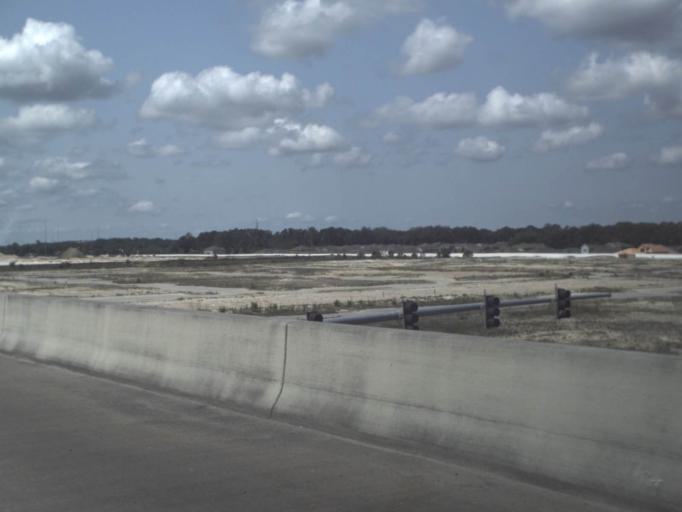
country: US
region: Florida
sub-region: Duval County
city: Jacksonville
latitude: 30.3380
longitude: -81.5524
